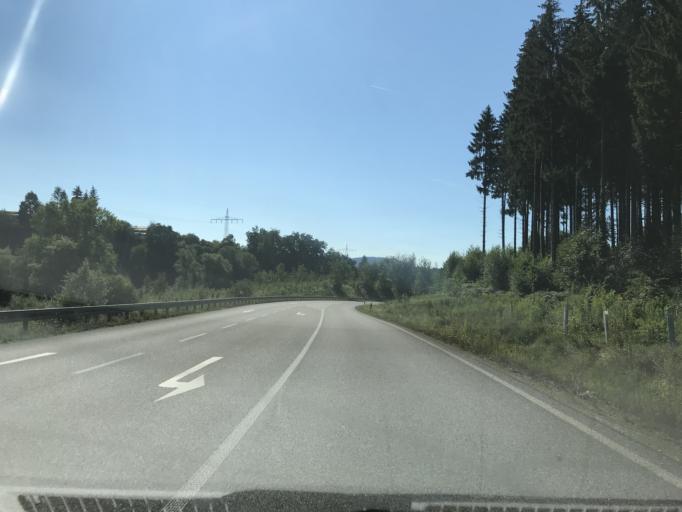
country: DE
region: Baden-Wuerttemberg
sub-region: Freiburg Region
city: Rheinfelden (Baden)
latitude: 47.5841
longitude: 7.7902
